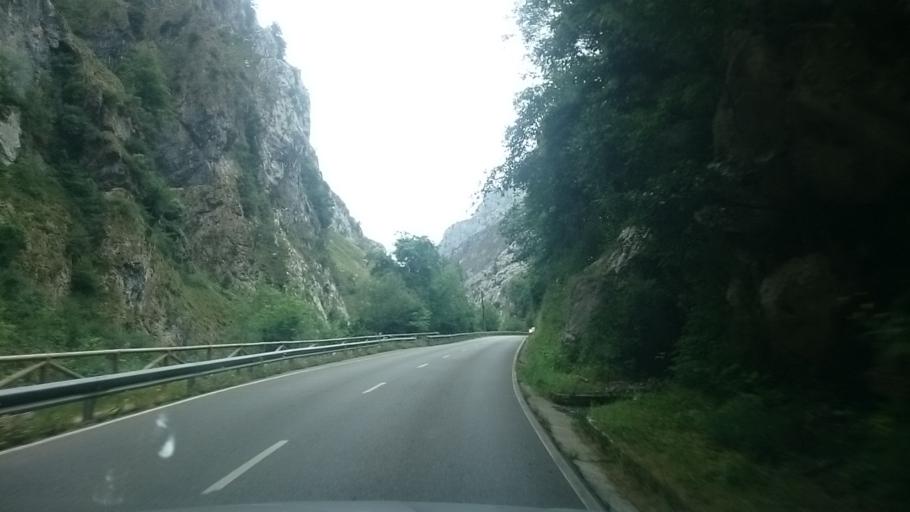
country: ES
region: Asturias
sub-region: Province of Asturias
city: Carrena
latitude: 43.2657
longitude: -4.8320
